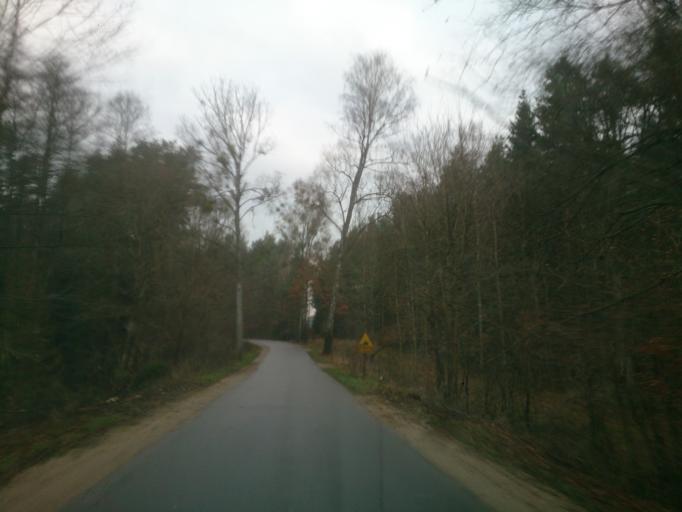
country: PL
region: Pomeranian Voivodeship
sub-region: Powiat slupski
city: Kepice
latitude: 54.1325
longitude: 16.9325
